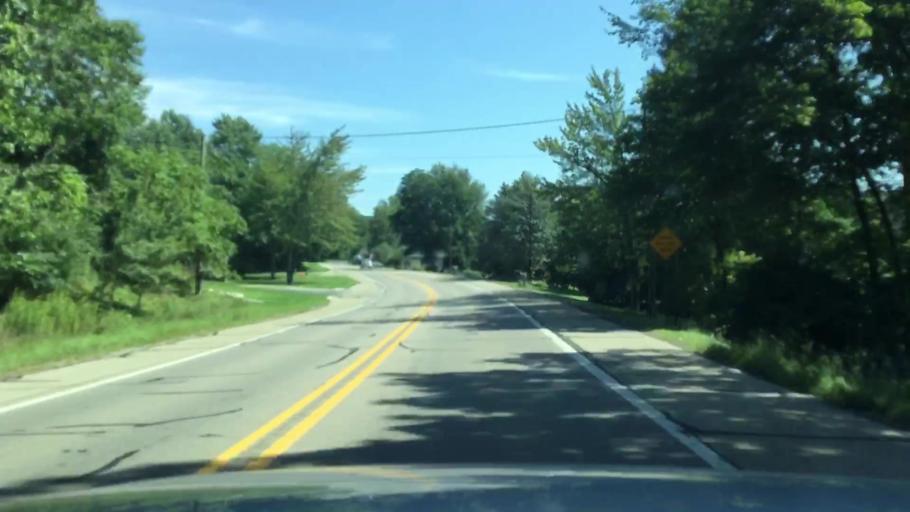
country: US
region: Michigan
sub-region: Washtenaw County
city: Manchester
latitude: 42.0618
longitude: -84.1198
